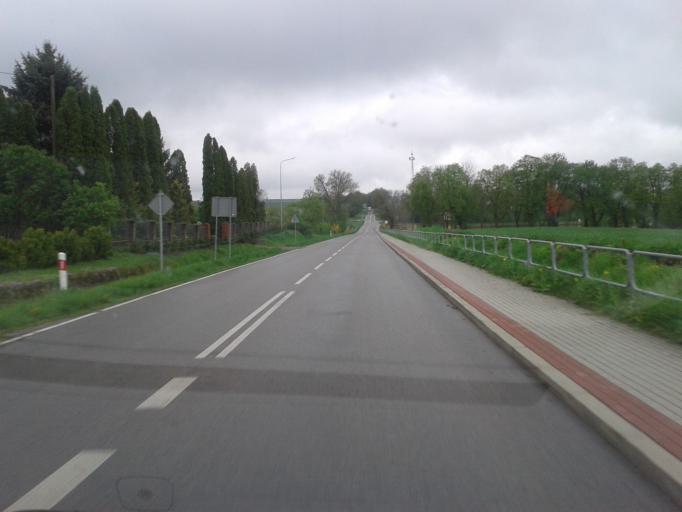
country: PL
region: Lublin Voivodeship
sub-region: Powiat tomaszowski
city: Telatyn
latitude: 50.5273
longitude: 23.9156
